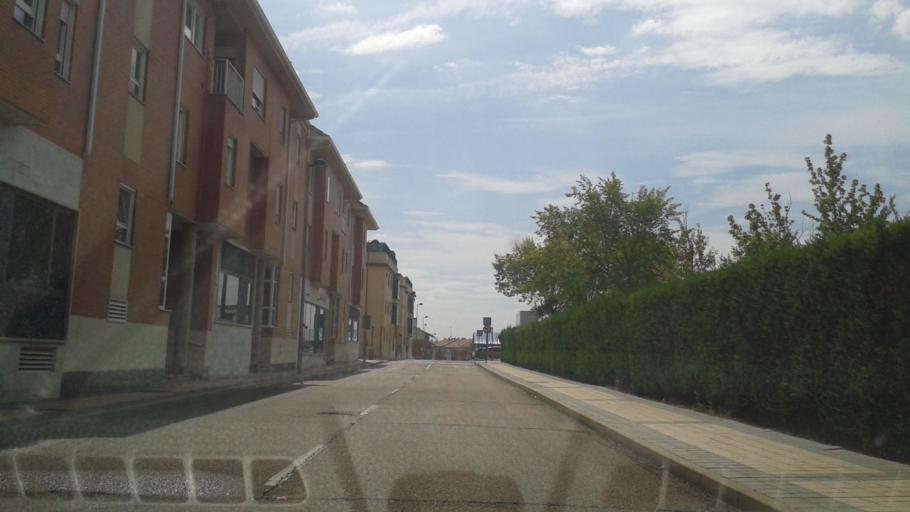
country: ES
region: Castille and Leon
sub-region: Provincia de Valladolid
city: Arroyo
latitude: 41.6289
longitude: -4.7760
